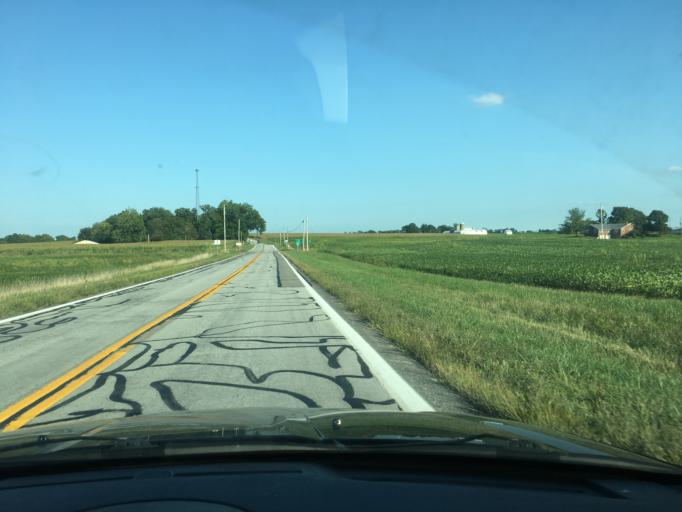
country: US
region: Ohio
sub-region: Logan County
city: West Liberty
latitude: 40.2486
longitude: -83.7865
